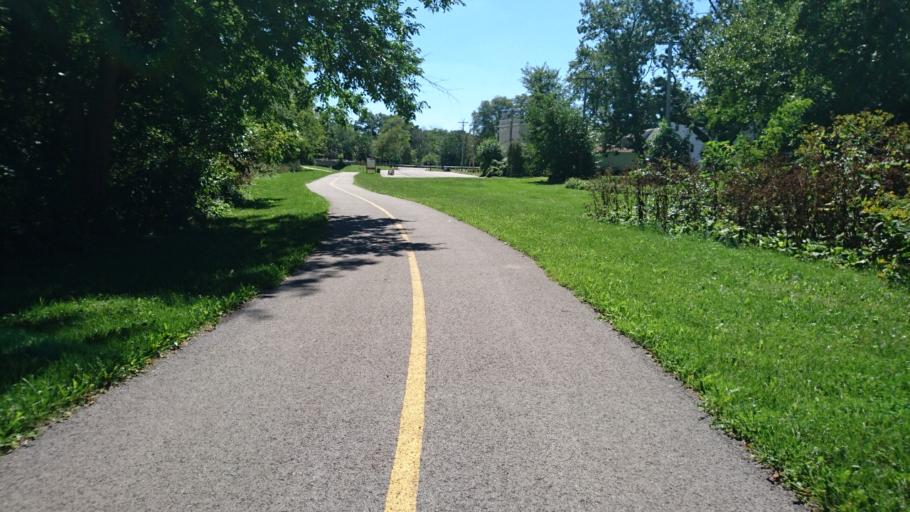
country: US
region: Illinois
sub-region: Cook County
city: Chicago Heights
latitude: 41.5076
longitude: -87.6450
